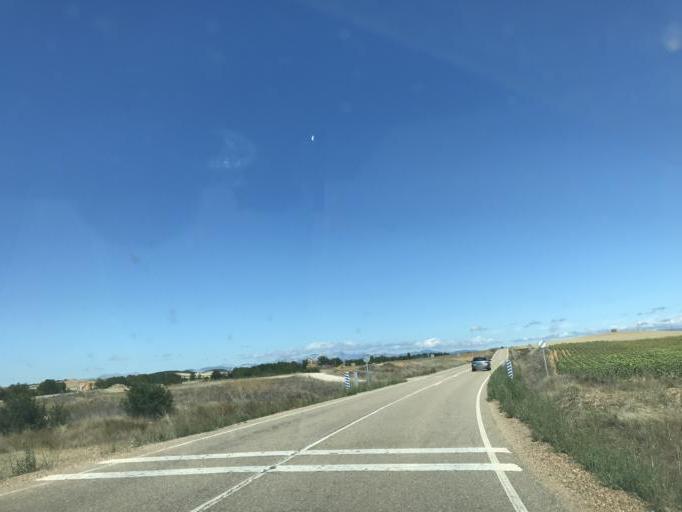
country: ES
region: Castille and Leon
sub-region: Provincia de Palencia
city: Herrera de Pisuerga
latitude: 42.6189
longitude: -4.3599
